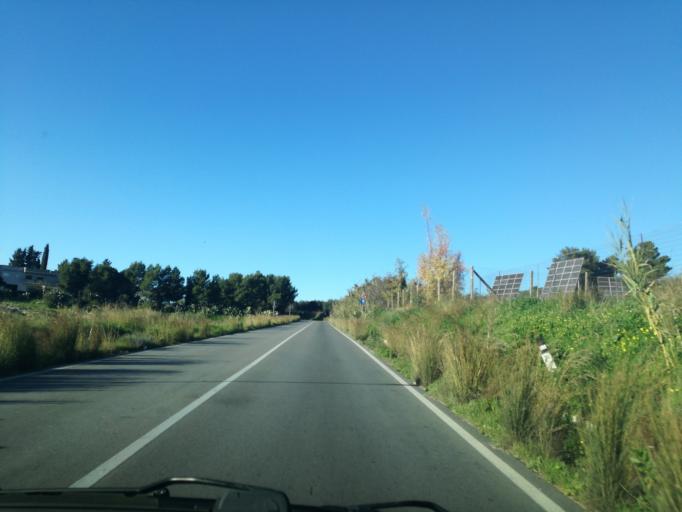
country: IT
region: Sicily
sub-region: Provincia di Caltanissetta
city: Gela
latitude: 37.1093
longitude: 14.1598
